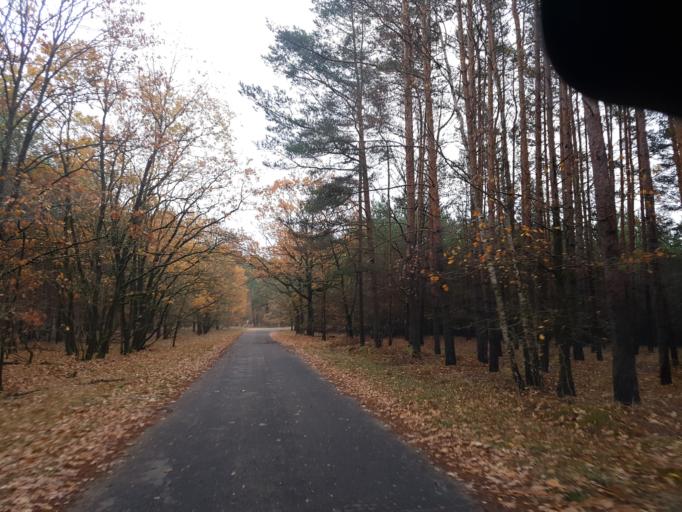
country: DE
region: Brandenburg
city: Treuenbrietzen
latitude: 52.1074
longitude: 12.9081
